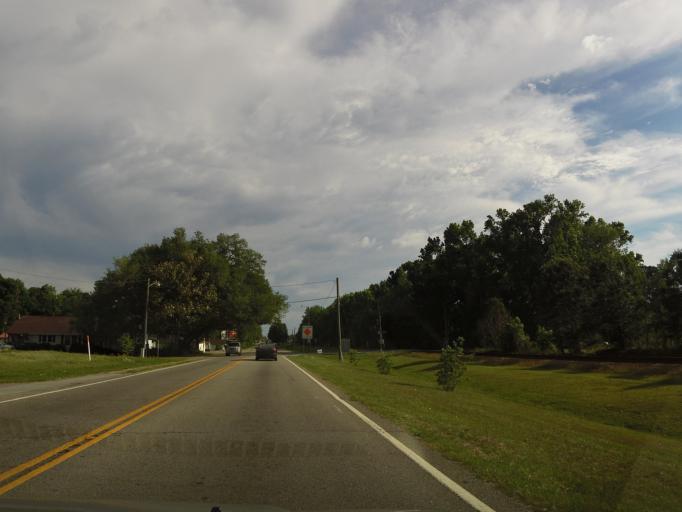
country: US
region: South Carolina
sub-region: Hampton County
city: Estill
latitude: 32.7646
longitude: -81.2411
